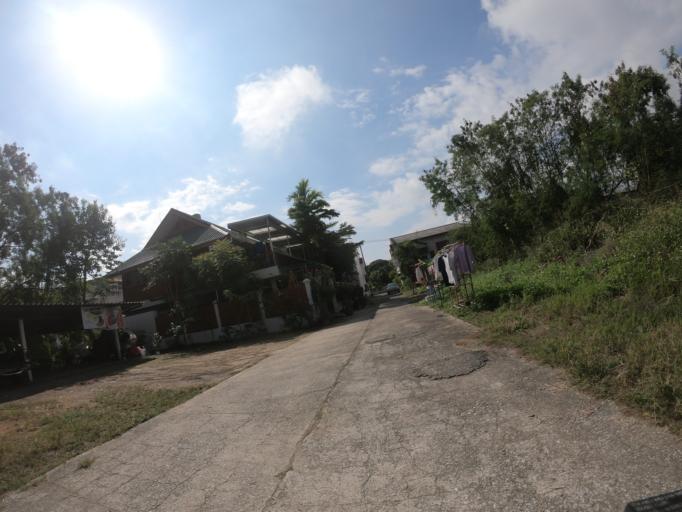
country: TH
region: Chiang Mai
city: Chiang Mai
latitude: 18.7363
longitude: 98.9562
